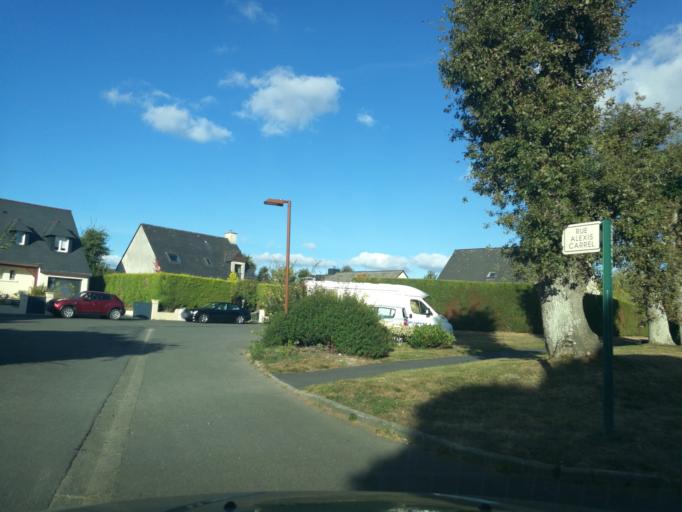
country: FR
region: Brittany
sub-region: Departement d'Ille-et-Vilaine
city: Bedee
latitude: 48.1764
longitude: -1.9380
